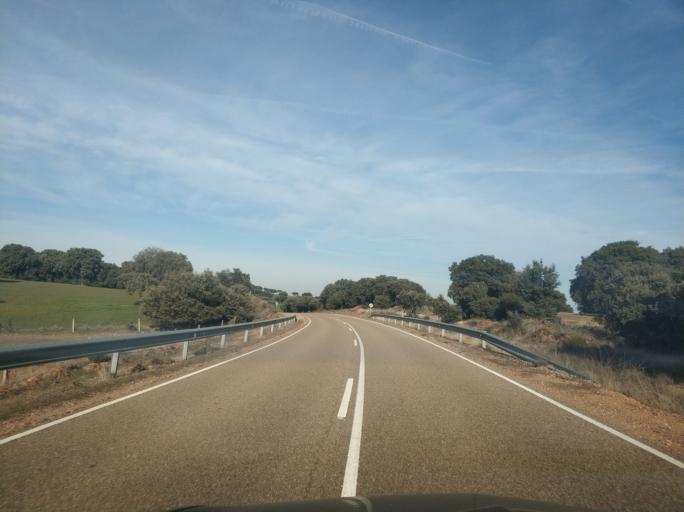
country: ES
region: Castille and Leon
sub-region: Provincia de Salamanca
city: Zarapicos
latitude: 41.0041
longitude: -5.8317
